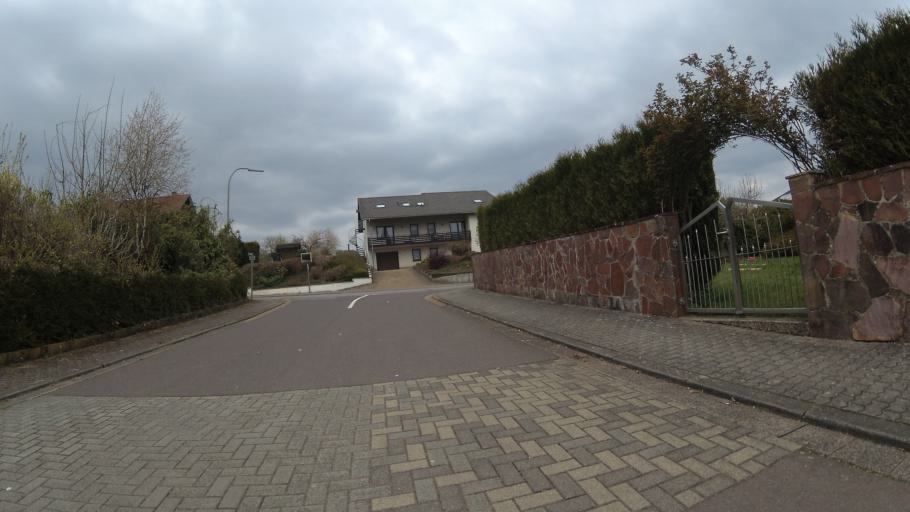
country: DE
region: Saarland
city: Merzig
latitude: 49.4342
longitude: 6.6118
